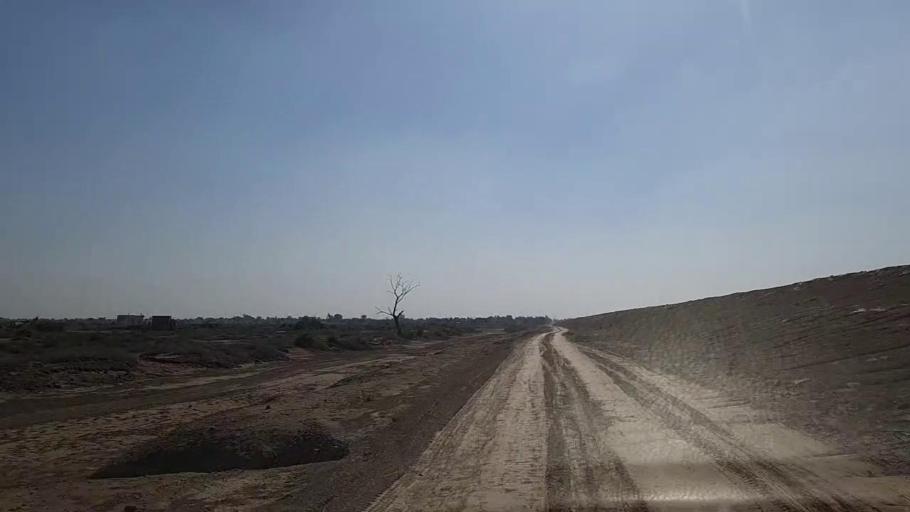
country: PK
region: Sindh
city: Daro Mehar
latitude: 24.7919
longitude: 68.0769
